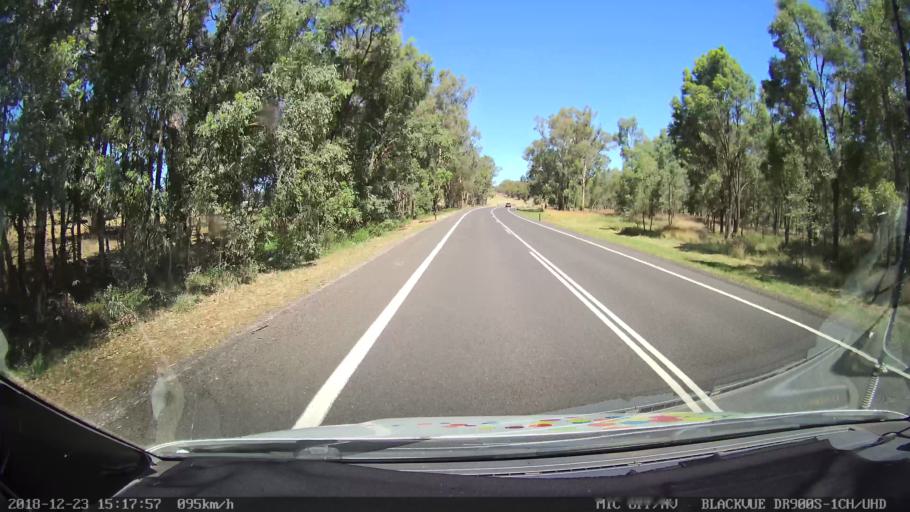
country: AU
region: New South Wales
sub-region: Tamworth Municipality
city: Manilla
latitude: -30.8125
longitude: 150.7663
